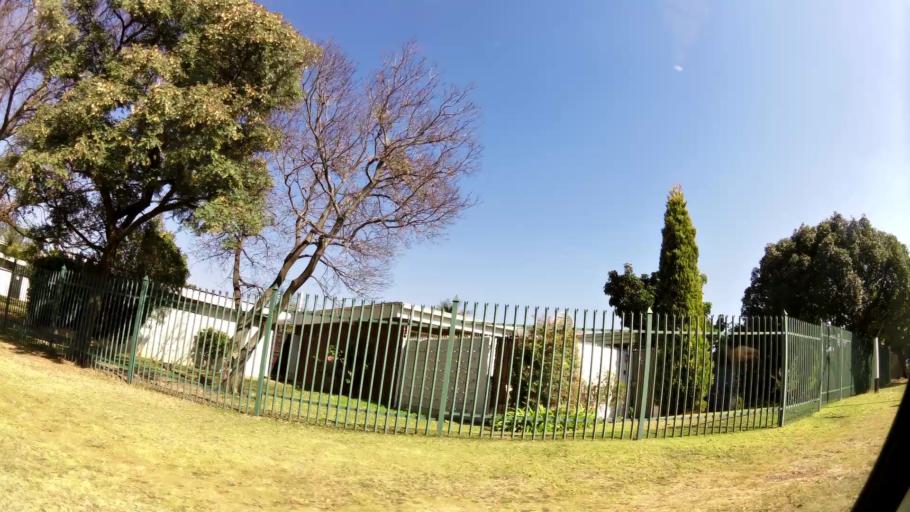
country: ZA
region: Gauteng
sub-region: City of Tshwane Metropolitan Municipality
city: Pretoria
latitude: -25.7573
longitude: 28.2592
